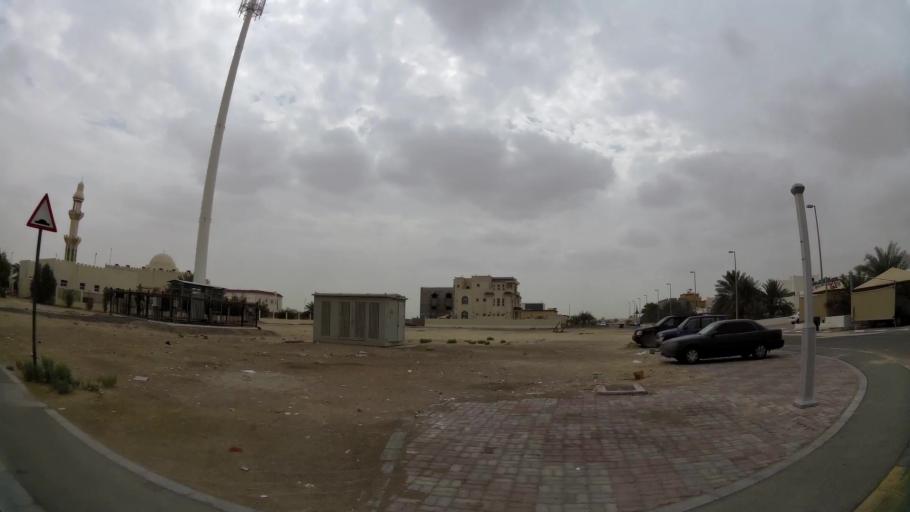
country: AE
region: Abu Dhabi
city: Abu Dhabi
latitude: 24.3435
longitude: 54.6434
